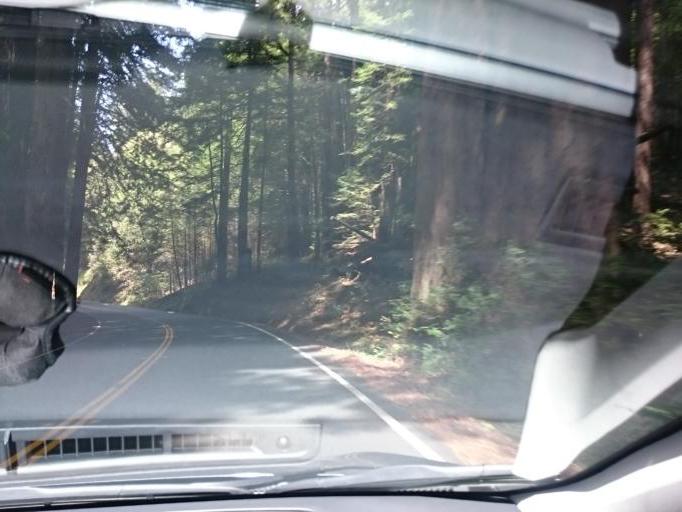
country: US
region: California
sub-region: Mendocino County
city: Boonville
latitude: 39.1586
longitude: -123.6375
